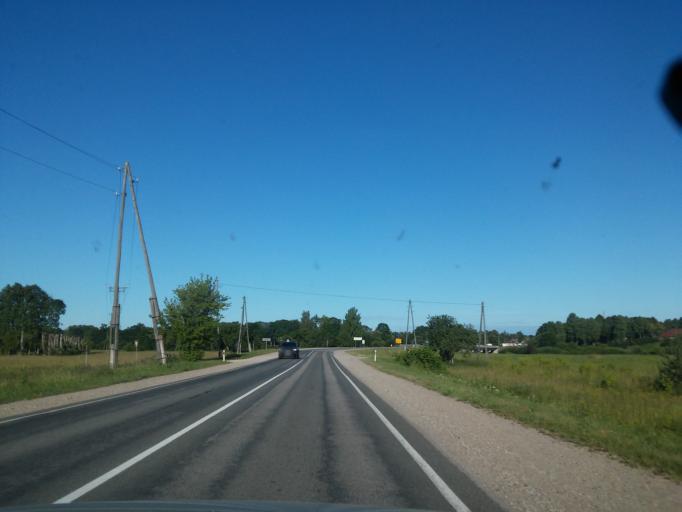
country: LV
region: Skrunda
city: Skrunda
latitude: 56.6706
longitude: 22.0319
